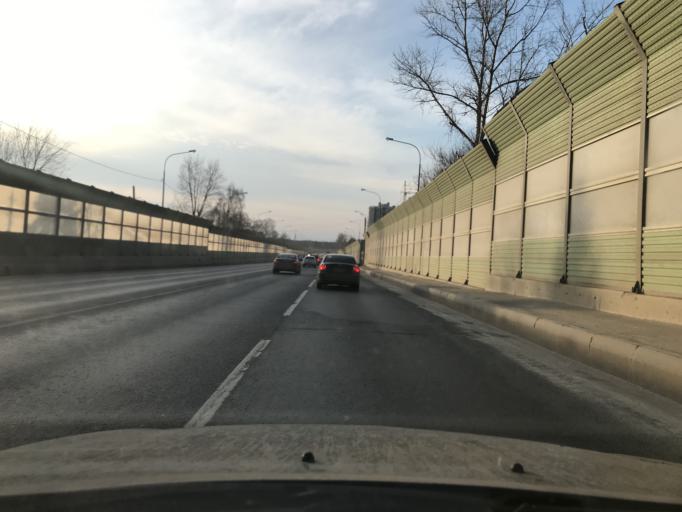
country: RU
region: Kaluga
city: Mstikhino
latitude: 54.5339
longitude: 36.1658
